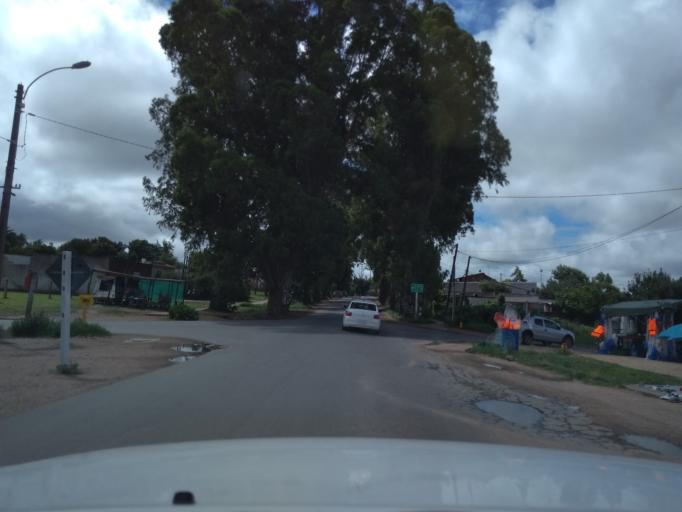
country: UY
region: Canelones
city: Pando
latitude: -34.7172
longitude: -55.9662
